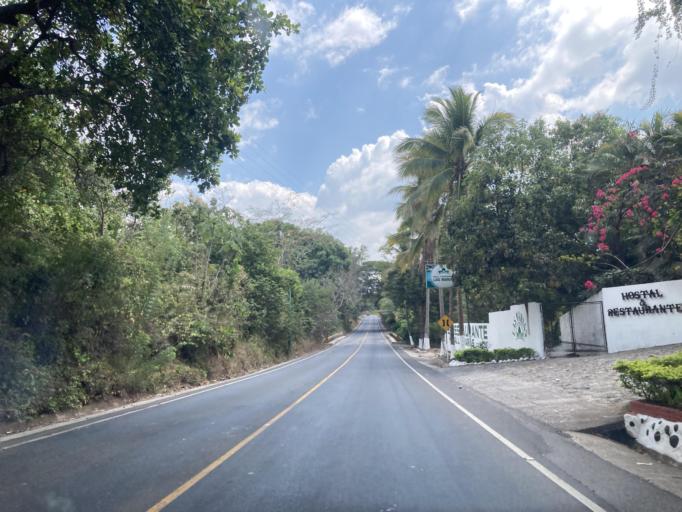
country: GT
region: Santa Rosa
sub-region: Municipio de Taxisco
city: Taxisco
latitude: 14.0652
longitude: -90.4563
